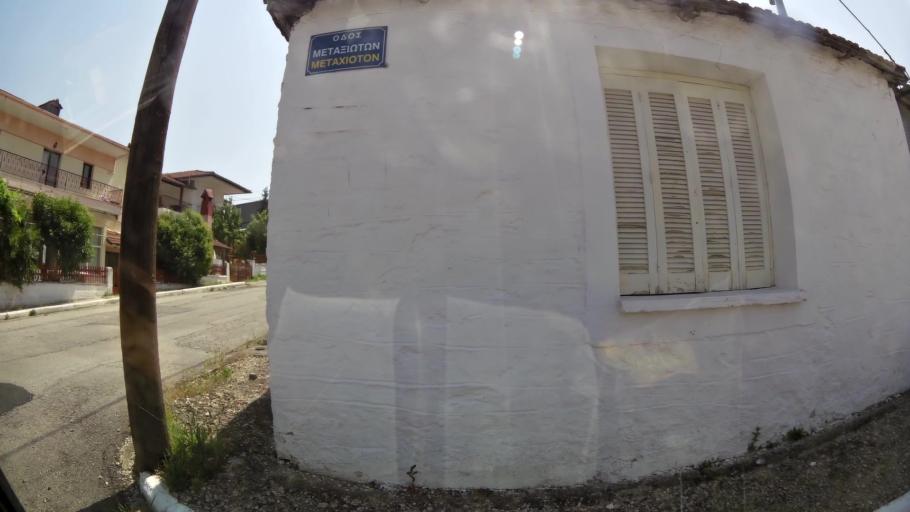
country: GR
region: West Macedonia
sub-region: Nomos Kozanis
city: Koila
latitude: 40.3291
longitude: 21.7937
